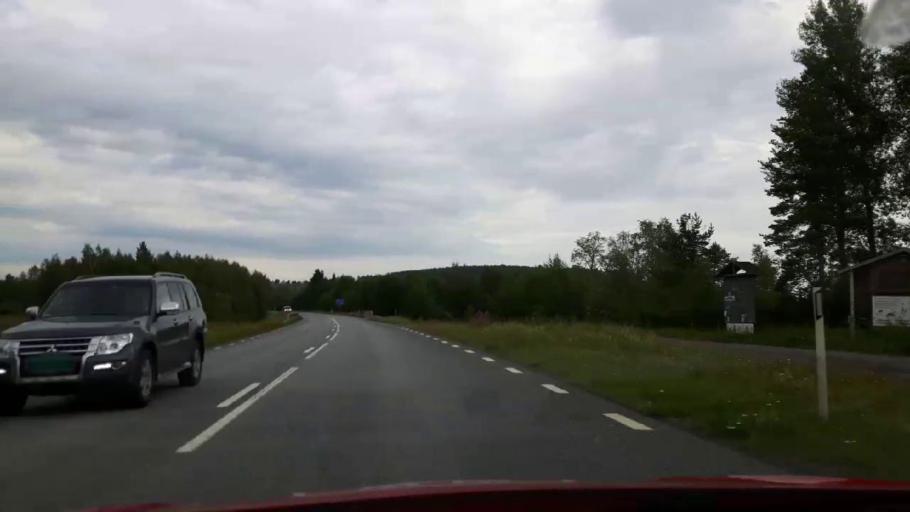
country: SE
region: Jaemtland
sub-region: Stroemsunds Kommun
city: Stroemsund
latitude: 63.5437
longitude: 15.3700
